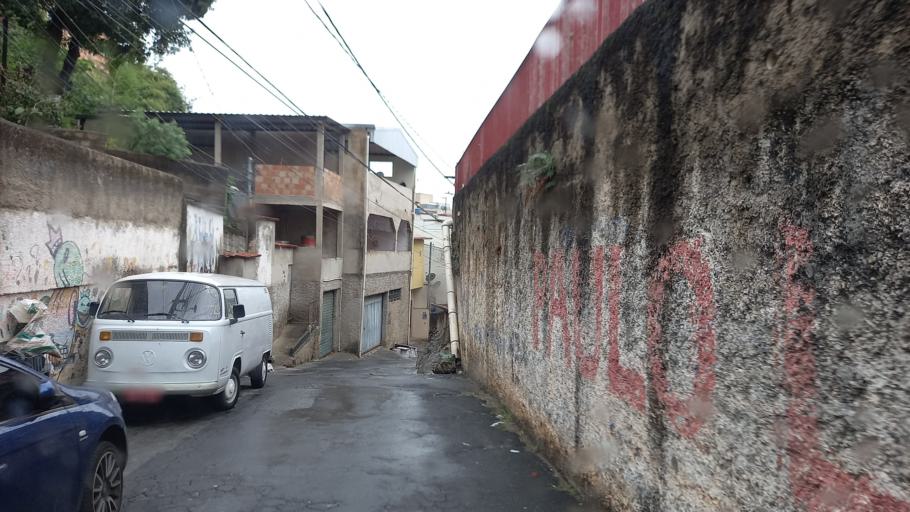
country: BR
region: Minas Gerais
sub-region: Belo Horizonte
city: Belo Horizonte
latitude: -19.9104
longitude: -43.9052
